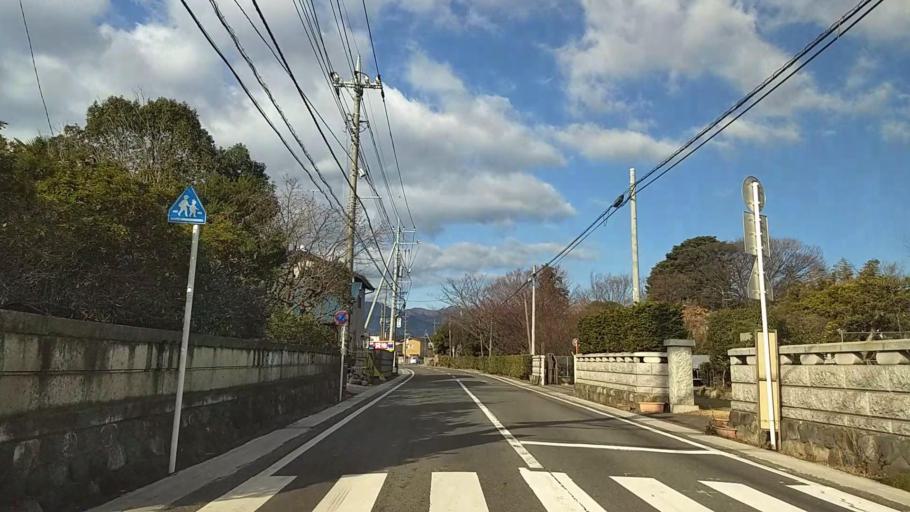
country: JP
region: Kanagawa
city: Atsugi
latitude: 35.4168
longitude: 139.3572
